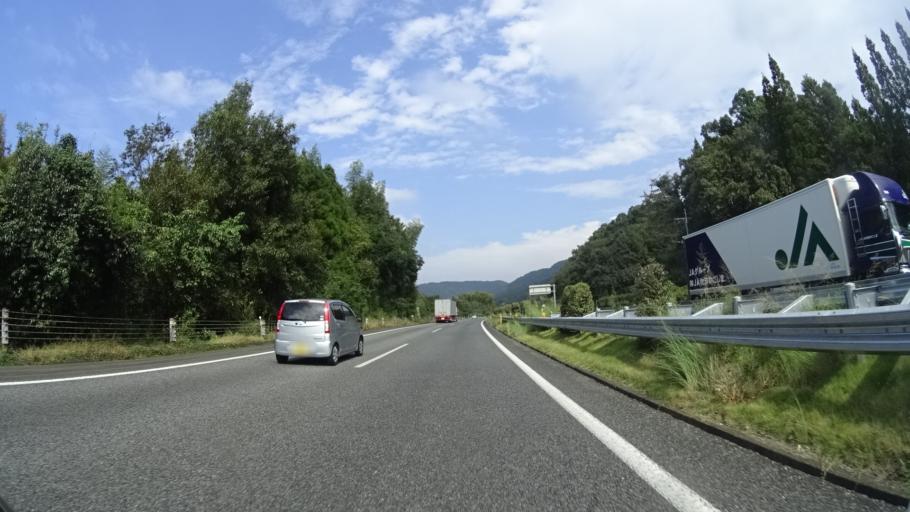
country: JP
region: Kumamoto
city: Matsubase
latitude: 32.5942
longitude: 130.7168
